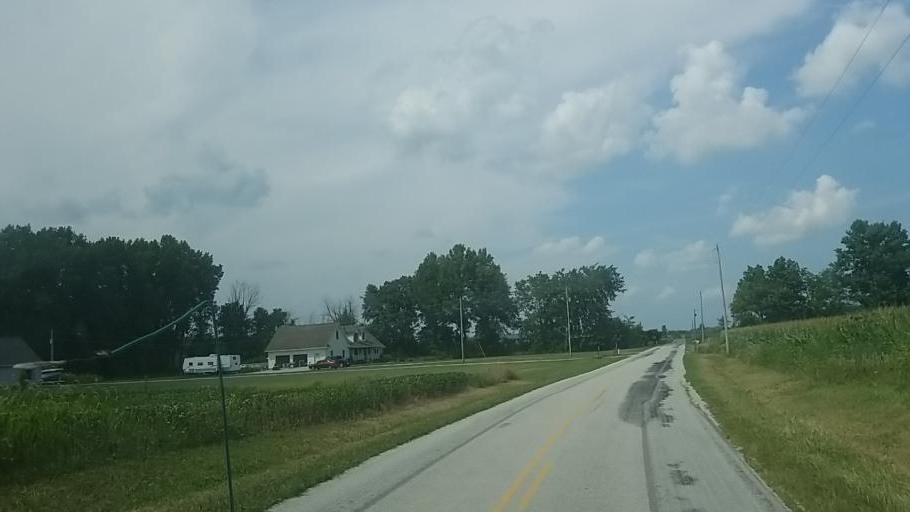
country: US
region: Ohio
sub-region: Hardin County
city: Kenton
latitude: 40.7481
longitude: -83.6024
